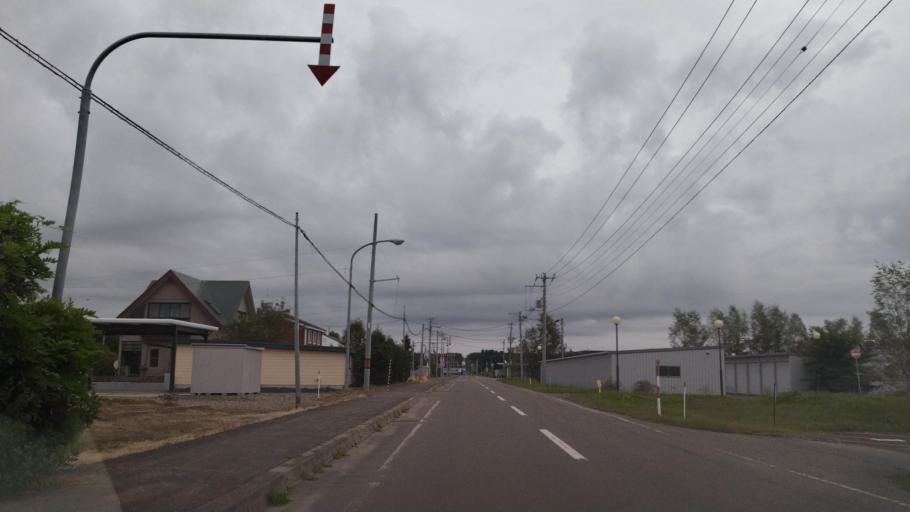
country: JP
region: Hokkaido
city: Otofuke
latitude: 43.2255
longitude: 143.2887
